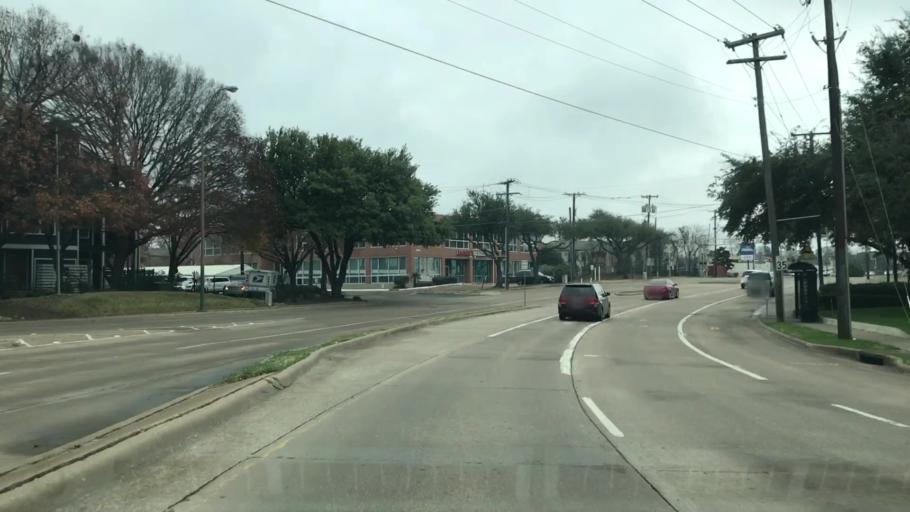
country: US
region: Texas
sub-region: Dallas County
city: Richardson
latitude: 32.8974
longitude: -96.7180
